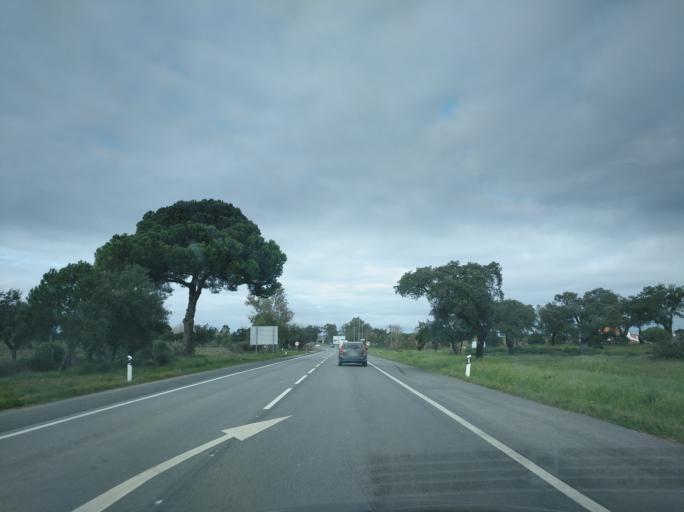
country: PT
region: Setubal
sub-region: Grandola
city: Grandola
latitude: 38.2005
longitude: -8.5636
